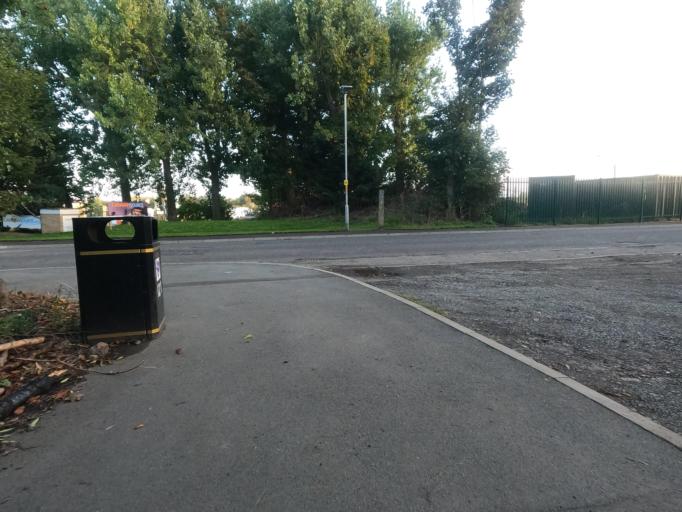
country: GB
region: England
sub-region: Northumberland
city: Seaton Delaval
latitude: 55.0790
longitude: -1.5332
